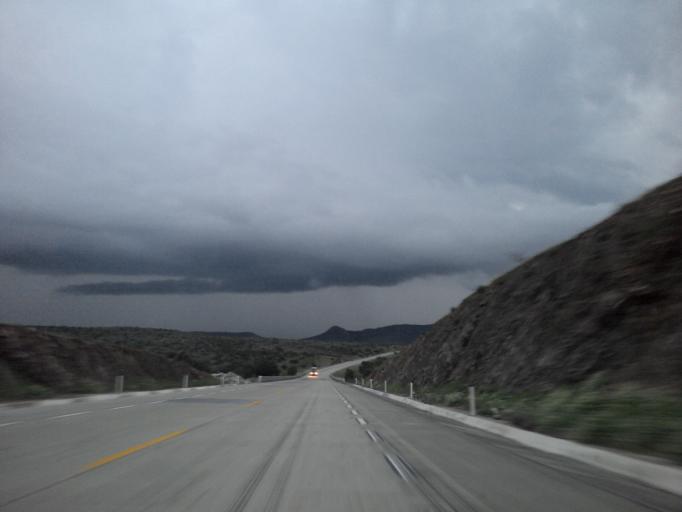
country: MX
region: Zacatecas
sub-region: Cuauhtemoc
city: Piedra Gorda
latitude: 22.5834
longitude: -102.3959
